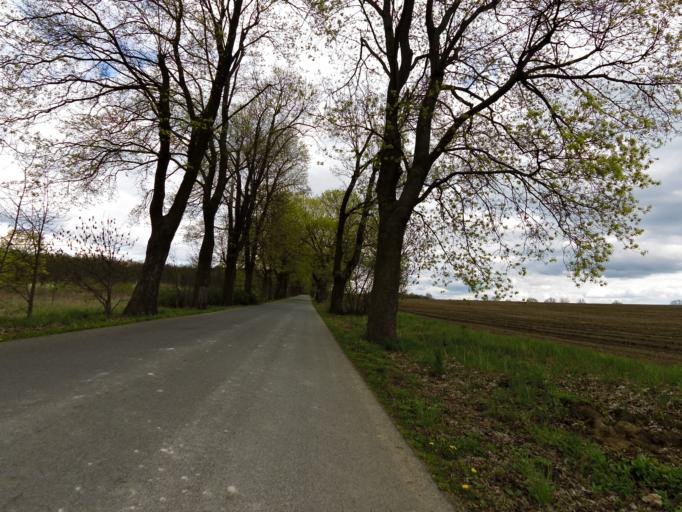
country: DE
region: Berlin
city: Lichtenrade
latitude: 52.3730
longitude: 13.4221
